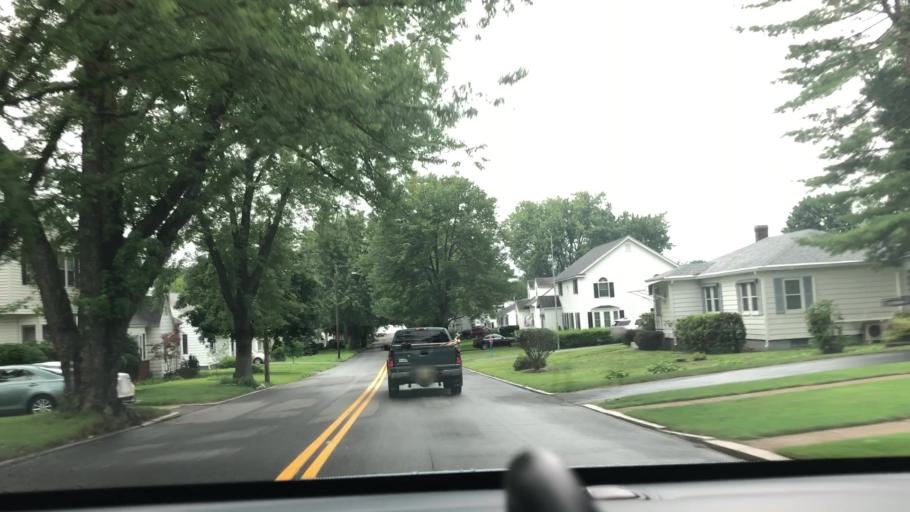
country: US
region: New Hampshire
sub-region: Hillsborough County
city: Manchester
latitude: 43.0009
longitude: -71.4810
